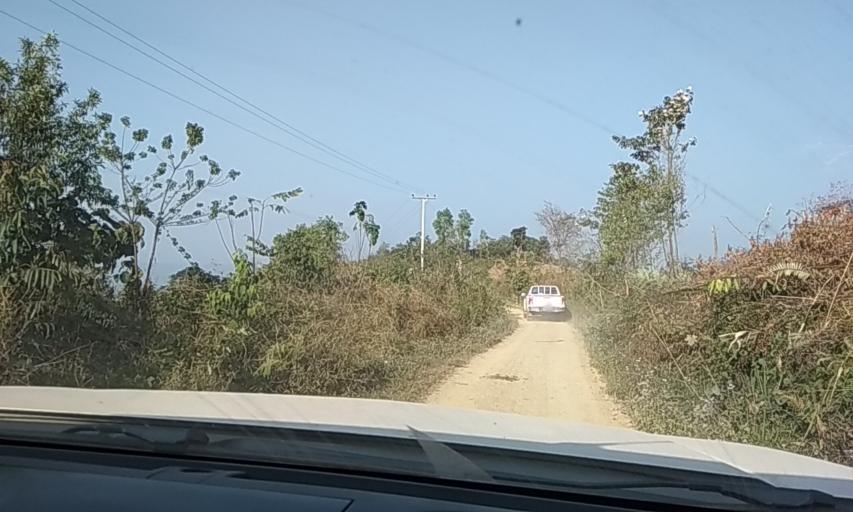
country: LA
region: Phongsali
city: Phongsali
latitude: 21.6631
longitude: 102.1786
